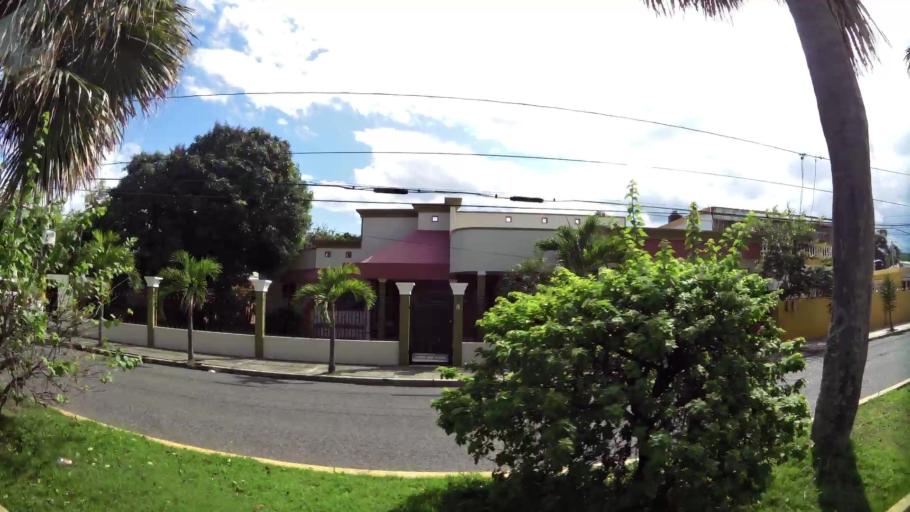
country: DO
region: La Vega
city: Concepcion de La Vega
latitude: 19.2176
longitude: -70.5208
